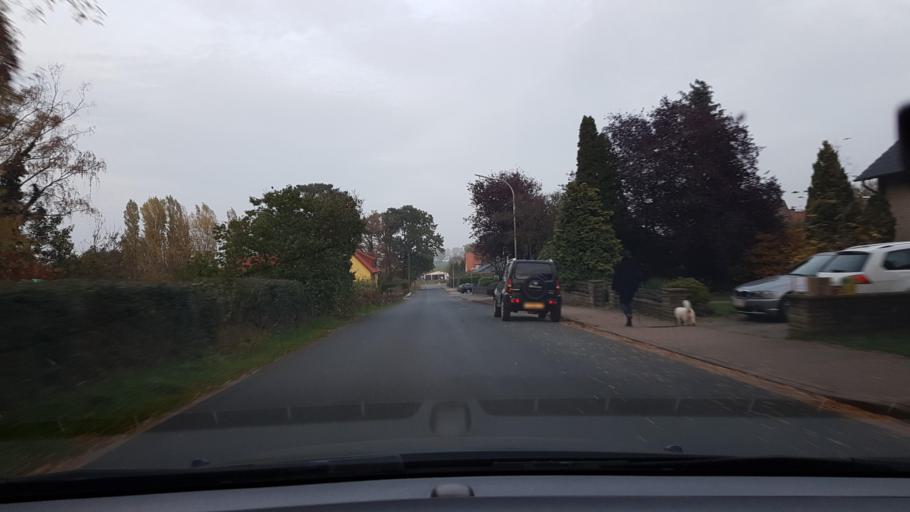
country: DE
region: Lower Saxony
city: Hagenburg
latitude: 52.4365
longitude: 9.3474
